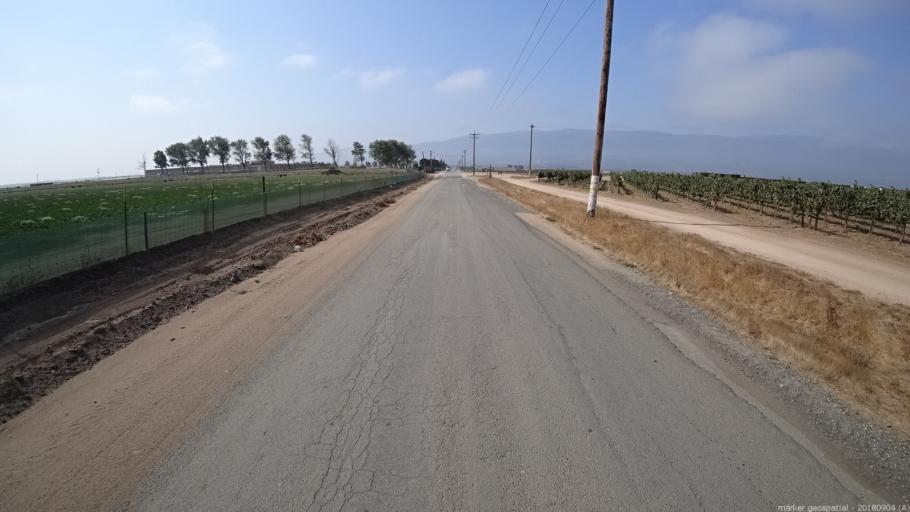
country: US
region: California
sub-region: Monterey County
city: Soledad
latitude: 36.4581
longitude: -121.3554
